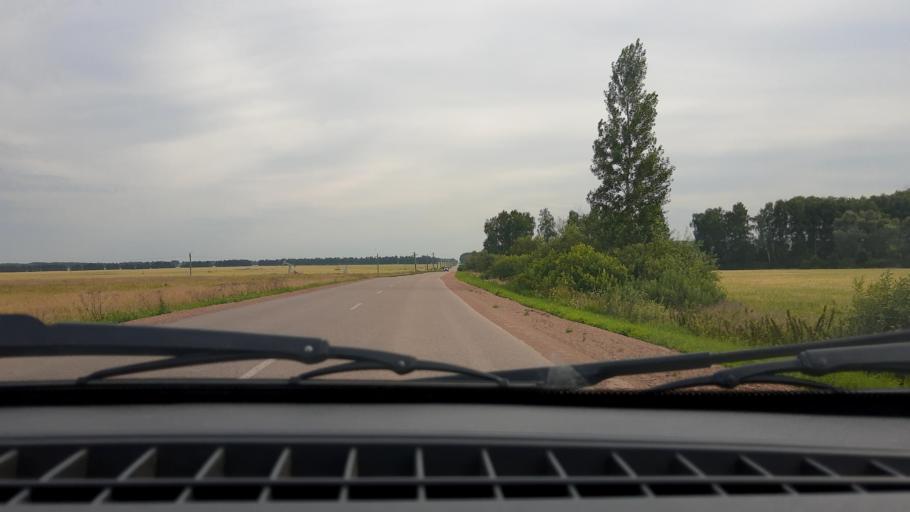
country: RU
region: Bashkortostan
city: Mikhaylovka
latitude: 54.8774
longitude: 55.8550
